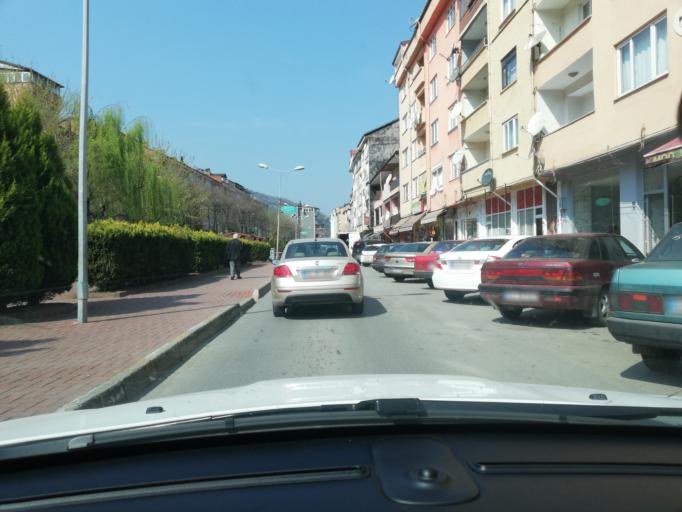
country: TR
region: Karabuk
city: Yenice
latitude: 41.2008
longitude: 32.3272
